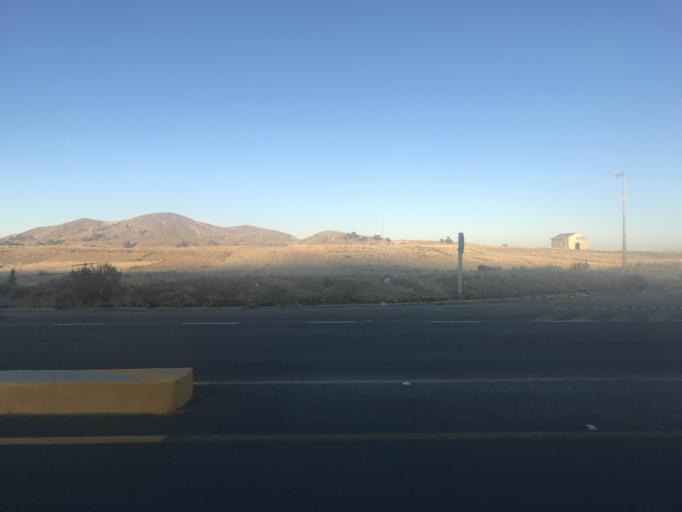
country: BO
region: La Paz
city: Huarina
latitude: -16.2252
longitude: -68.5833
